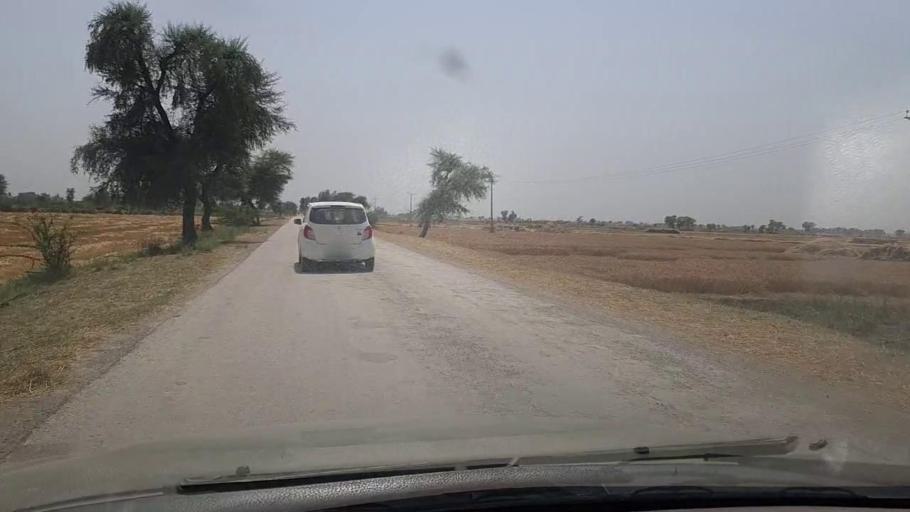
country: PK
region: Sindh
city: Miro Khan
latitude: 27.7203
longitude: 68.0687
